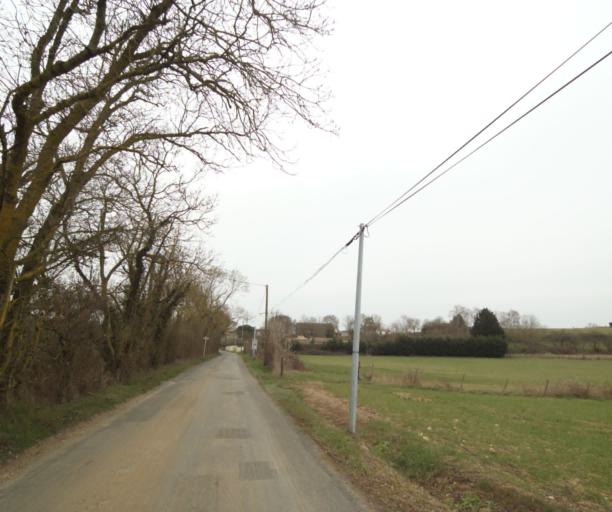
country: FR
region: Poitou-Charentes
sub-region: Departement des Deux-Sevres
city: Magne
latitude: 46.3304
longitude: -0.5247
